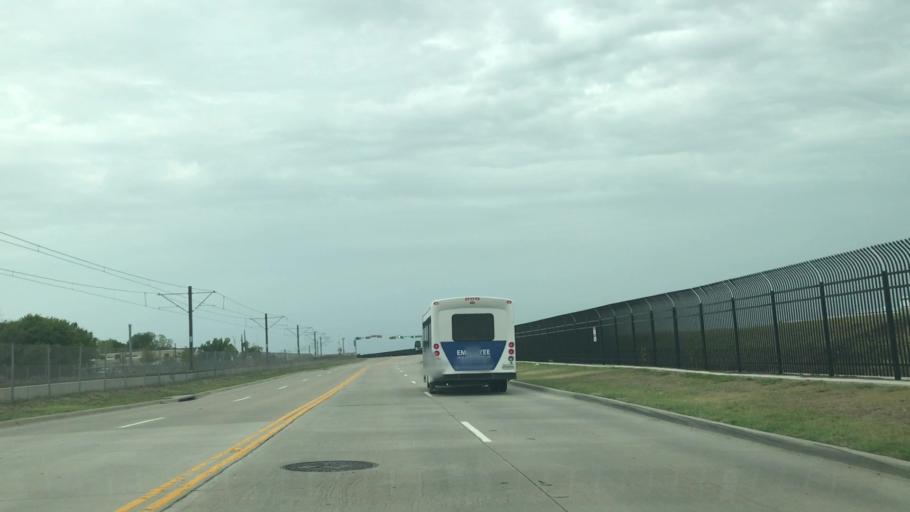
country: US
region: Texas
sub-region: Dallas County
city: University Park
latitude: 32.8356
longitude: -96.8478
